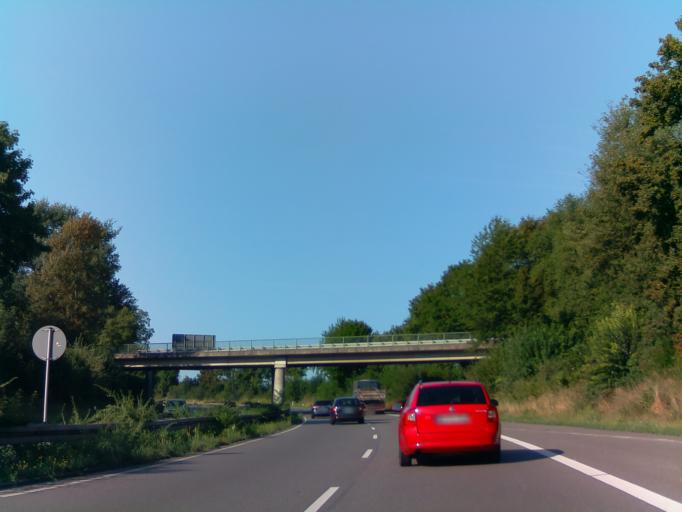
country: DE
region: Baden-Wuerttemberg
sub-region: Karlsruhe Region
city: Weinheim
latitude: 49.5568
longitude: 8.6465
